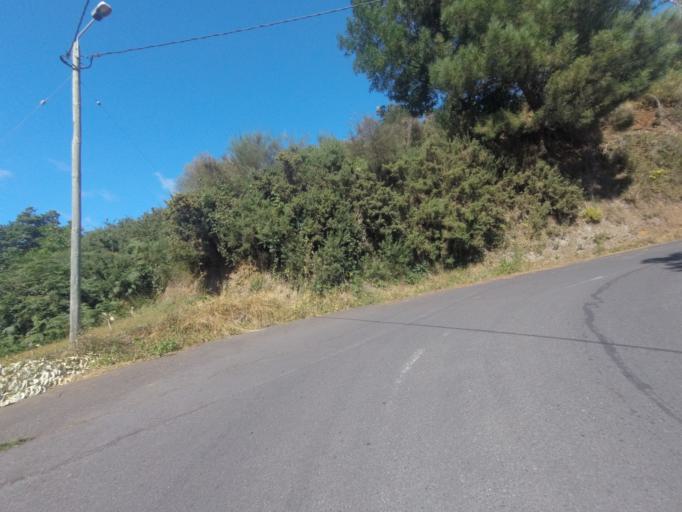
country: PT
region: Madeira
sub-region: Ribeira Brava
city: Campanario
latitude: 32.6941
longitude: -17.0185
